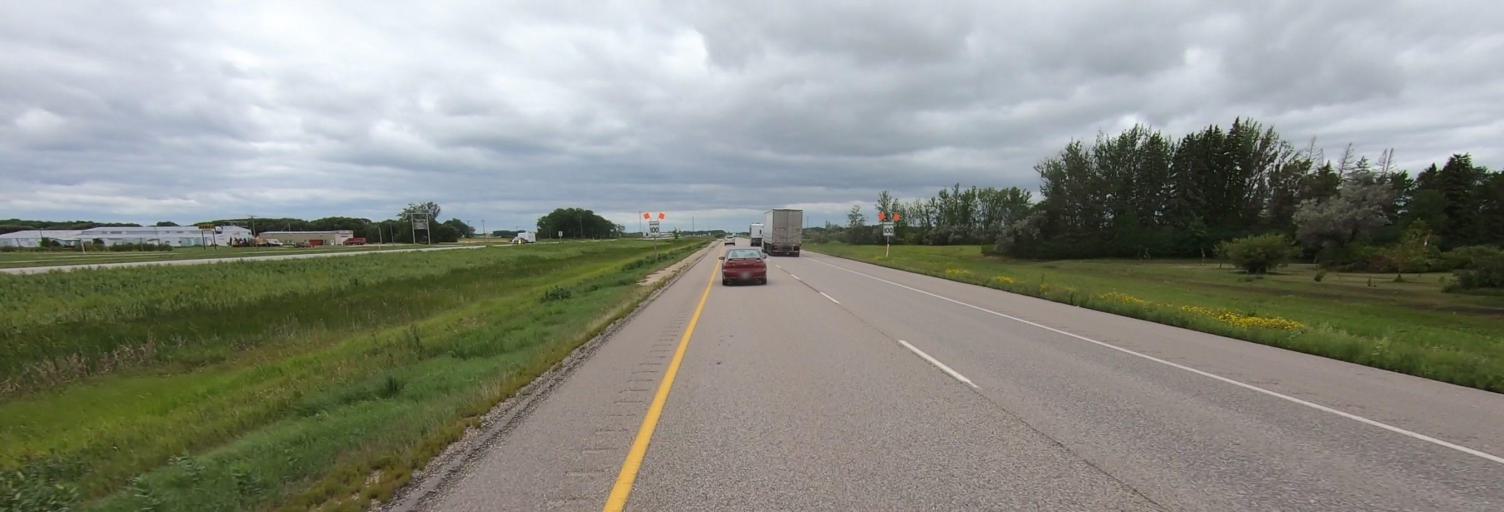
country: CA
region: Manitoba
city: Portage la Prairie
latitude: 49.9743
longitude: -98.1833
